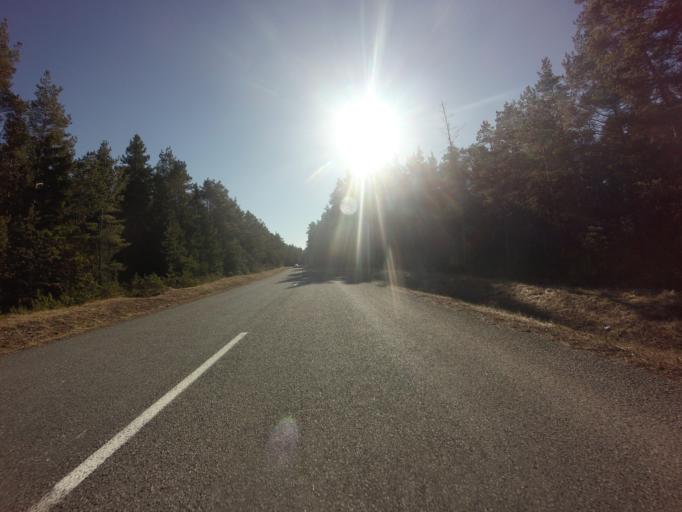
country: EE
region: Saare
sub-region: Kuressaare linn
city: Kuressaare
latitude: 58.5127
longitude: 22.3157
